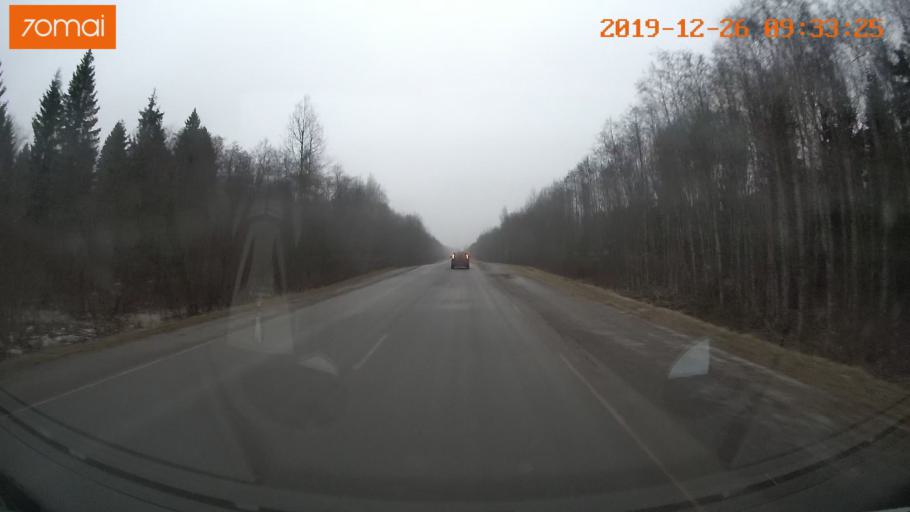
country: RU
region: Vologda
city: Vologda
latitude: 59.0896
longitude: 40.1010
